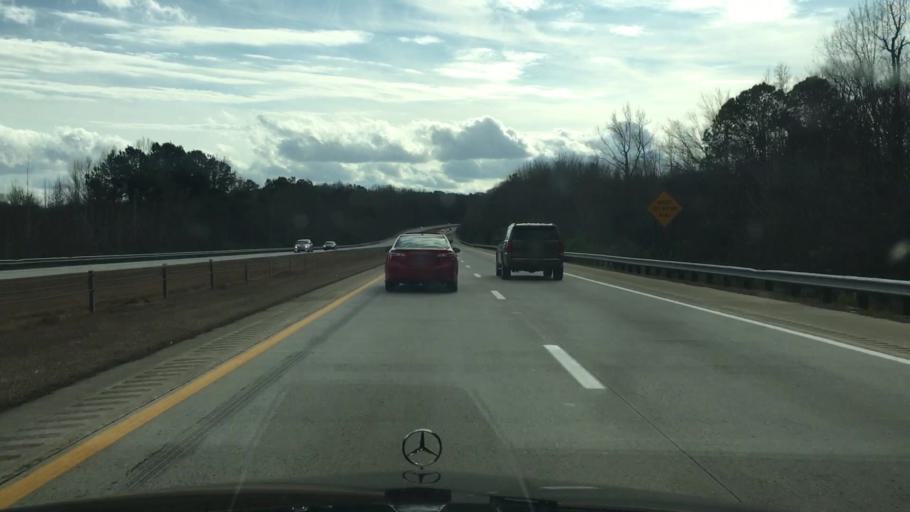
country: US
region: North Carolina
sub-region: Johnston County
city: Clayton
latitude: 35.5663
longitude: -78.5762
